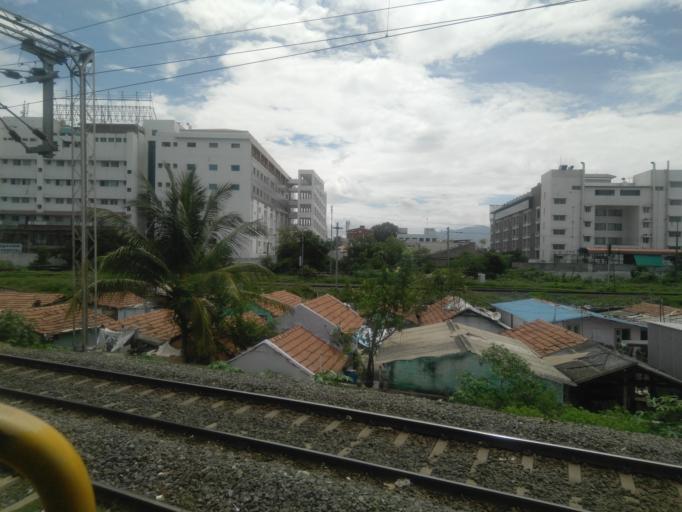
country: IN
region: Tamil Nadu
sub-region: Coimbatore
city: Coimbatore
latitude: 11.0267
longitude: 76.9537
